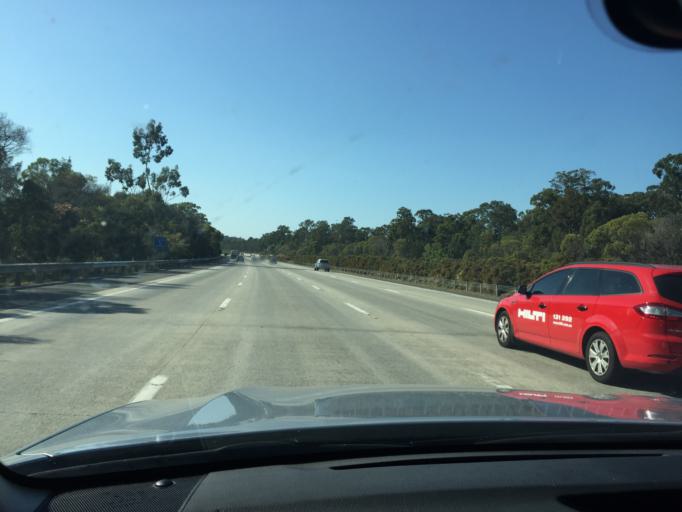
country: AU
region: Queensland
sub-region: Gold Coast
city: Ormeau Hills
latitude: -27.8118
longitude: 153.2721
